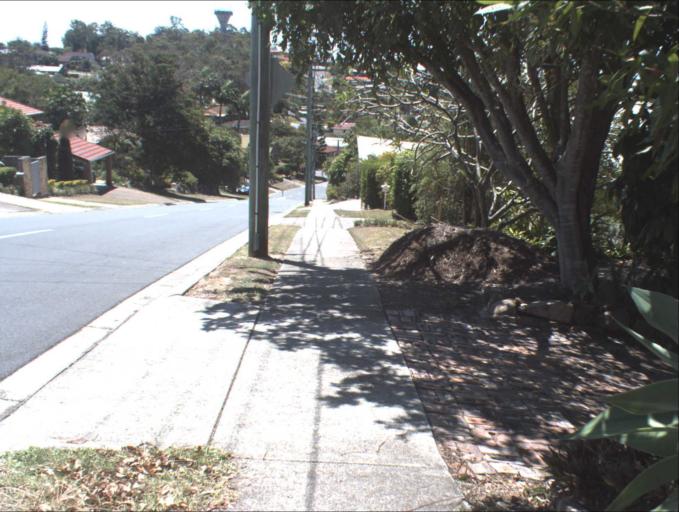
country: AU
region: Queensland
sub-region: Logan
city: Springwood
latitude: -27.6055
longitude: 153.1317
